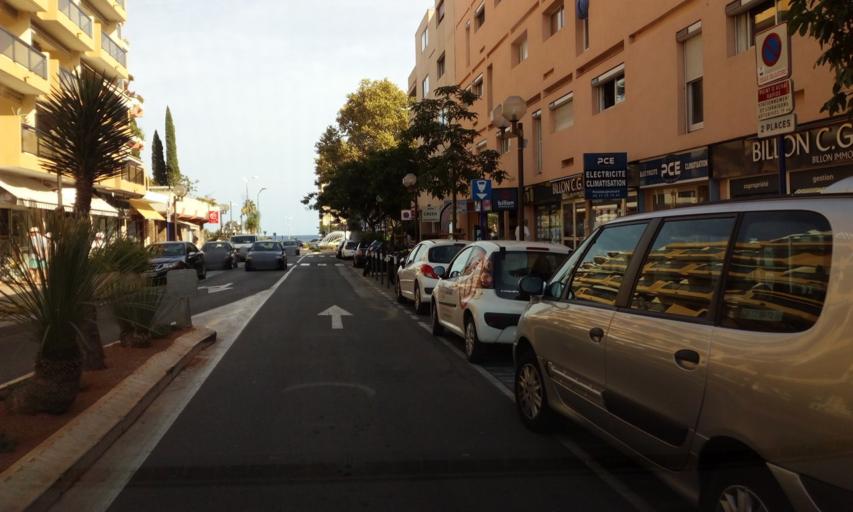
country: FR
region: Provence-Alpes-Cote d'Azur
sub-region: Departement du Var
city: Le Lavandou
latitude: 43.1369
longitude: 6.3650
